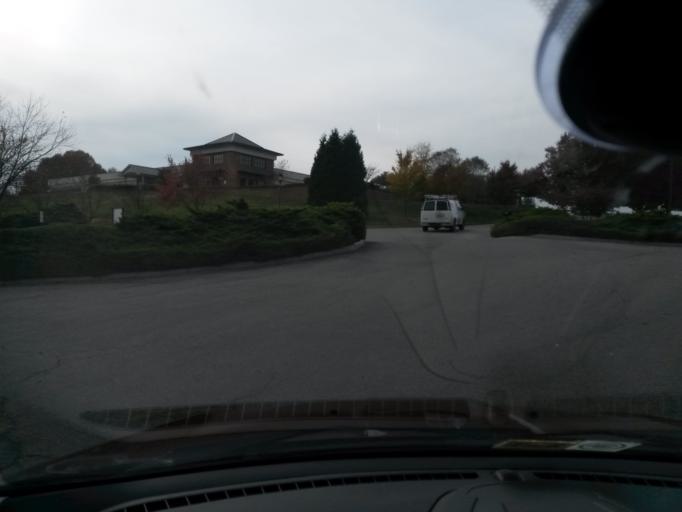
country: US
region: Virginia
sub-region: Roanoke County
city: Hollins
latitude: 37.3156
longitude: -79.9836
